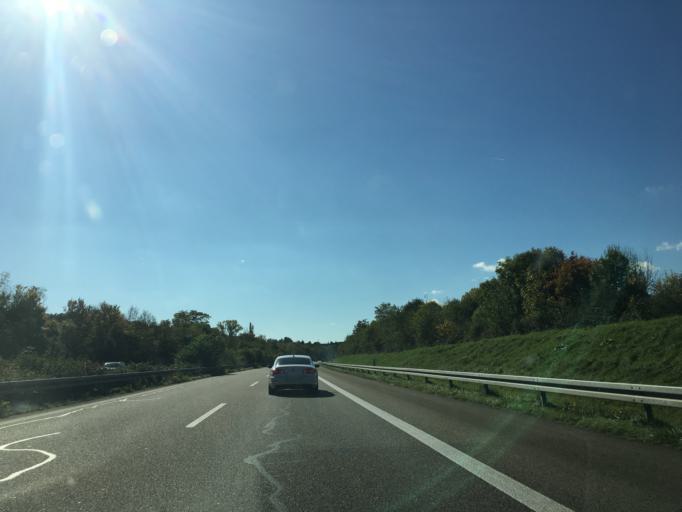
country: DE
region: Baden-Wuerttemberg
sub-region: Freiburg Region
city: Bad Bellingen
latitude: 47.7183
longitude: 7.5422
